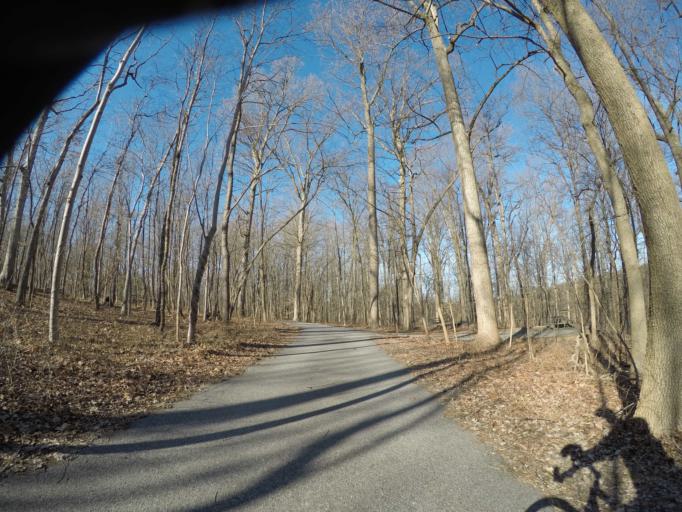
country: US
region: Maryland
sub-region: Howard County
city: Ellicott City
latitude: 39.2866
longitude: -76.7877
